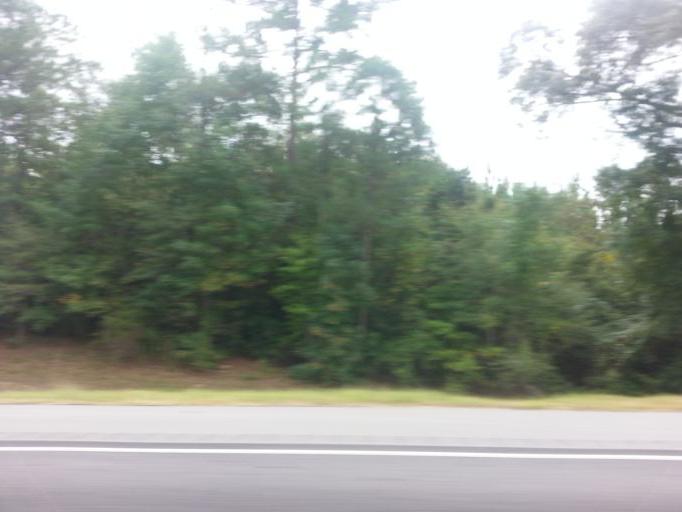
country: US
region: Alabama
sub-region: Conecuh County
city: Evergreen
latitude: 31.5217
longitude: -86.9074
